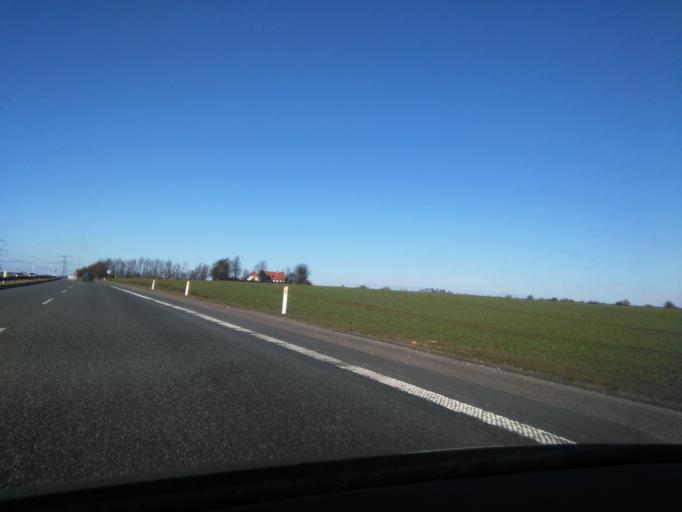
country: DK
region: Central Jutland
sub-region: Randers Kommune
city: Randers
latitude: 56.4964
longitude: 9.9793
